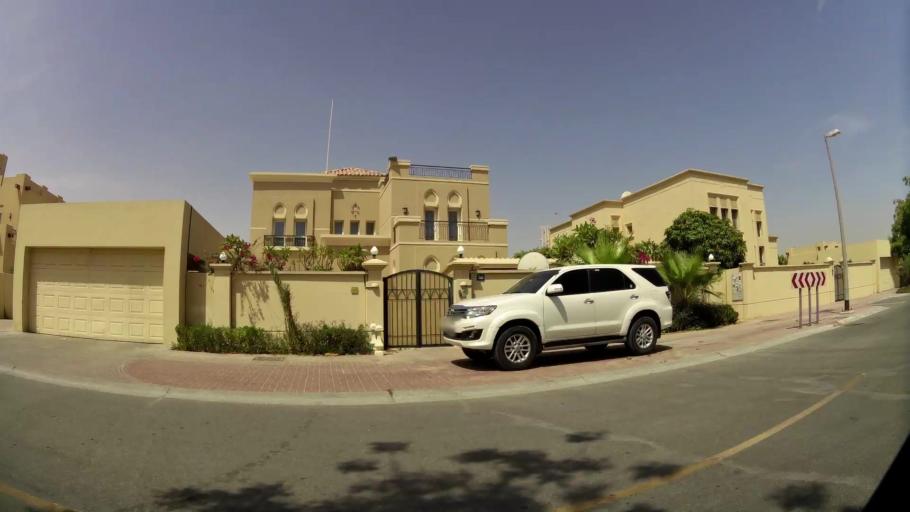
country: AE
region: Ash Shariqah
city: Sharjah
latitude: 25.1806
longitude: 55.4380
